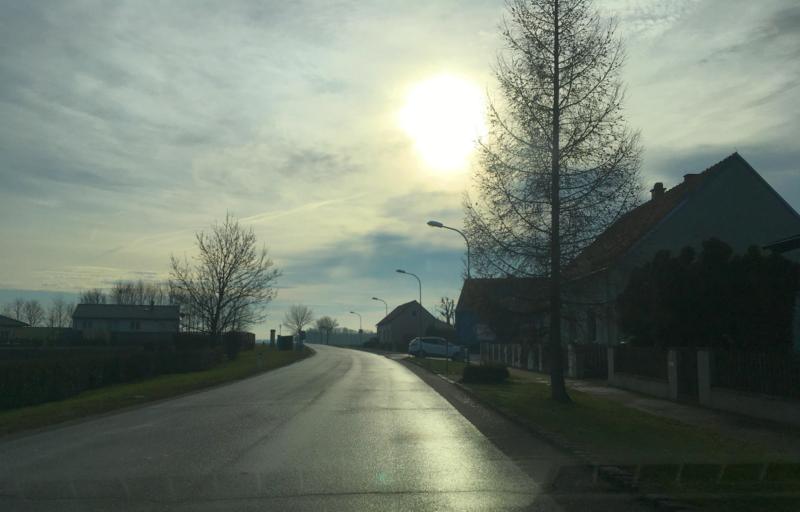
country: AT
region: Lower Austria
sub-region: Politischer Bezirk Ganserndorf
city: Haringsee
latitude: 48.1819
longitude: 16.7428
